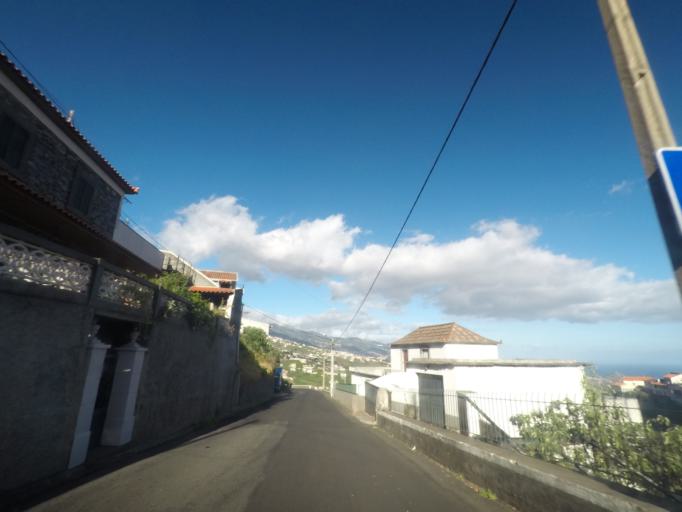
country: PT
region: Madeira
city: Camara de Lobos
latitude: 32.6659
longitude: -16.9910
